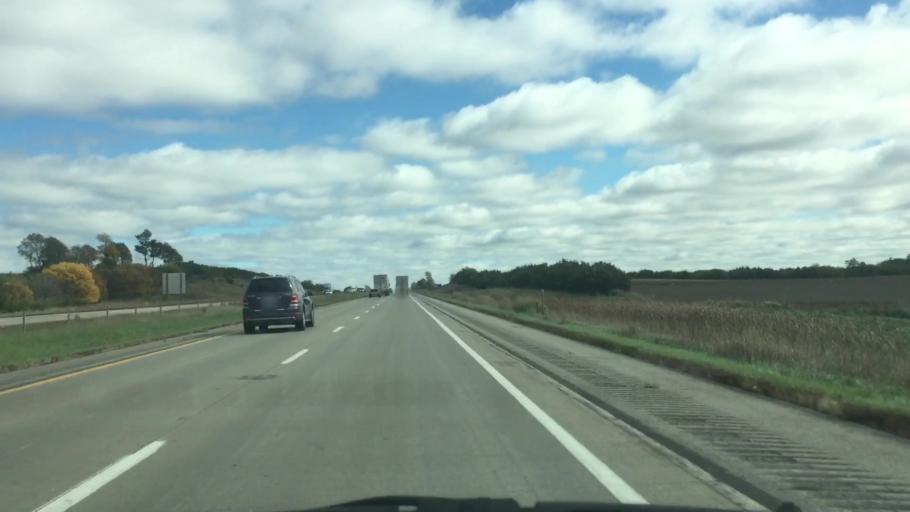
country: US
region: Iowa
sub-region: Jasper County
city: Newton
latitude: 41.6807
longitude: -92.9594
